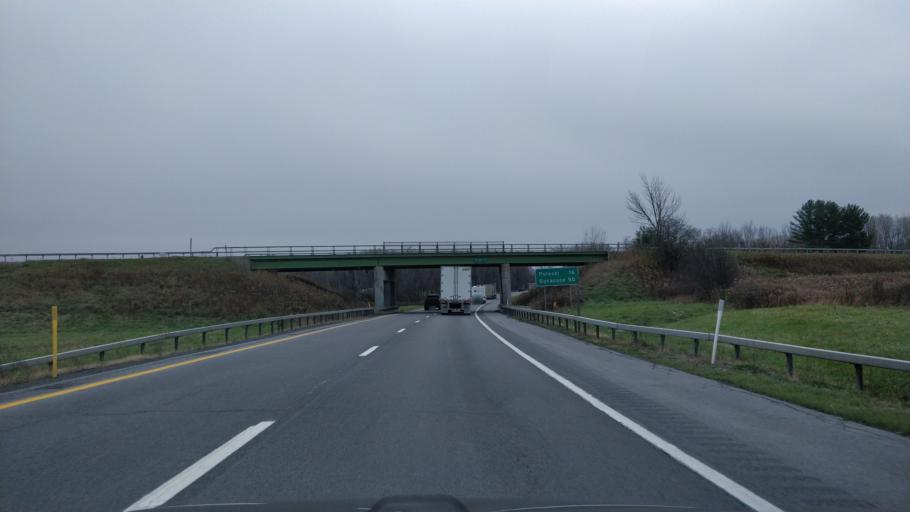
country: US
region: New York
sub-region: Jefferson County
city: Adams
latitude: 43.7782
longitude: -76.0440
